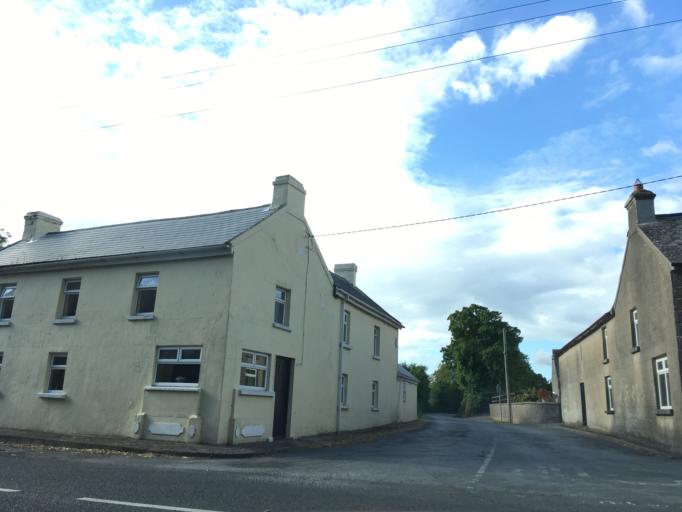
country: IE
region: Munster
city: Cahir
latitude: 52.2846
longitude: -7.9544
